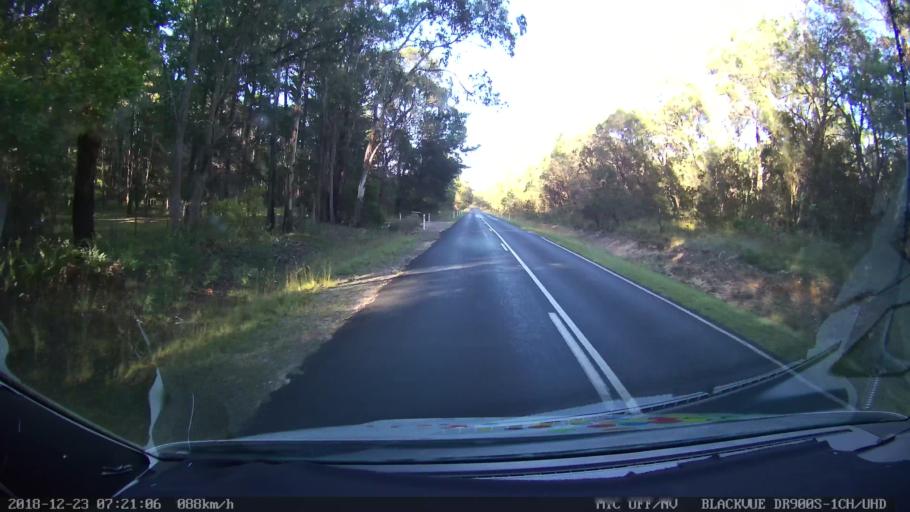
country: AU
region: New South Wales
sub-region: Bellingen
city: Dorrigo
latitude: -30.4956
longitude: 152.2679
